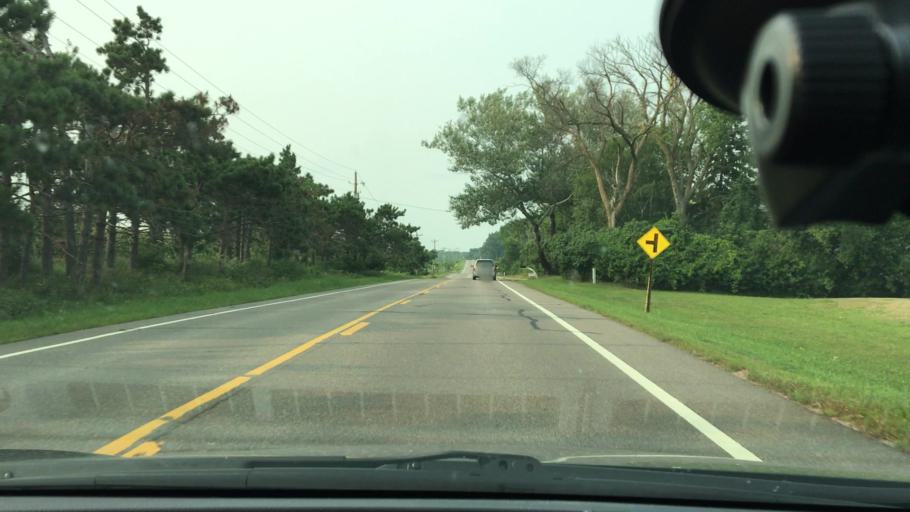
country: US
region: Minnesota
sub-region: Hennepin County
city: Champlin
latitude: 45.1789
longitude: -93.4623
